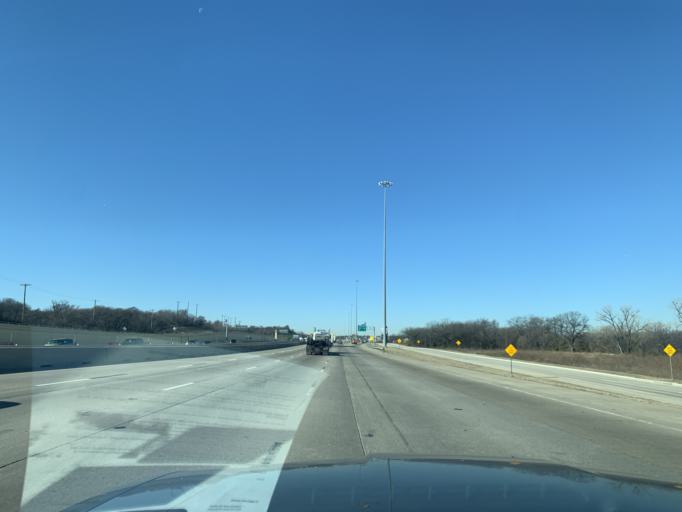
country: US
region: Texas
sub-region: Dallas County
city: Grand Prairie
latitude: 32.7594
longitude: -96.9803
